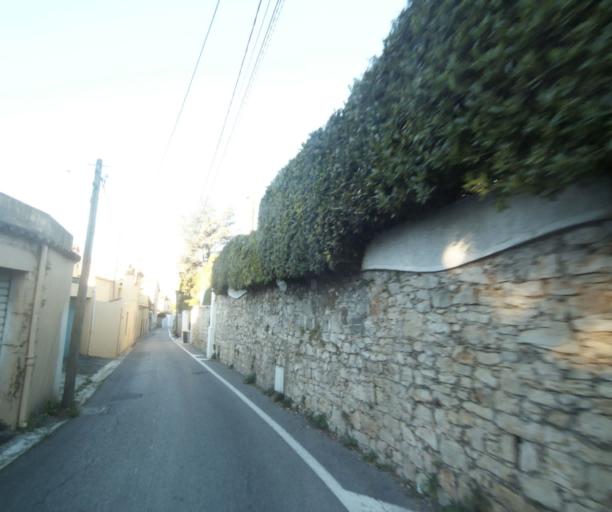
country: FR
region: Provence-Alpes-Cote d'Azur
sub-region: Departement des Alpes-Maritimes
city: Antibes
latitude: 43.5765
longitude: 7.0963
